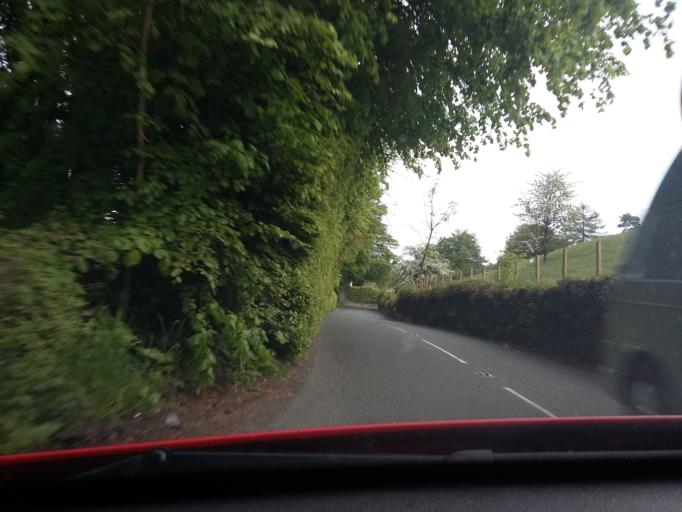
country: GB
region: England
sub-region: Cumbria
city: Windermere
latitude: 54.3879
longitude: -2.9142
